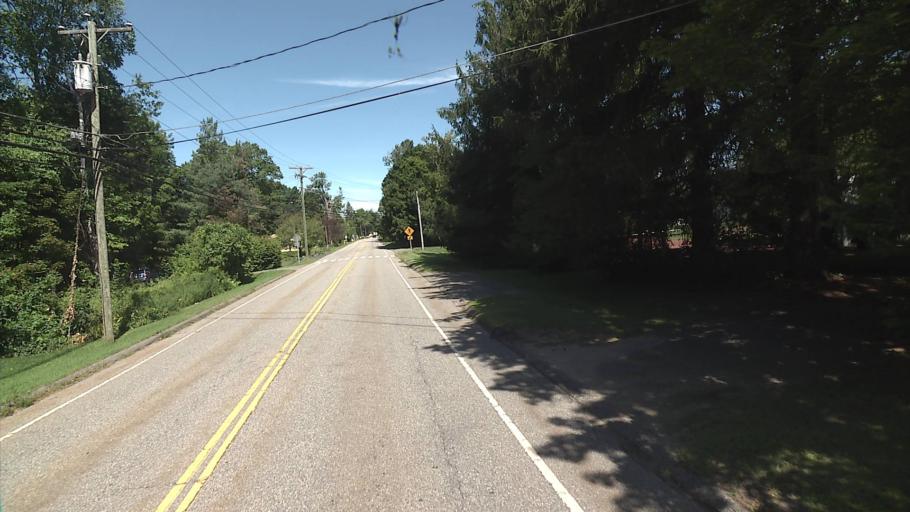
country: US
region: Connecticut
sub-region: Litchfield County
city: Litchfield
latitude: 41.7079
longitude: -73.2351
